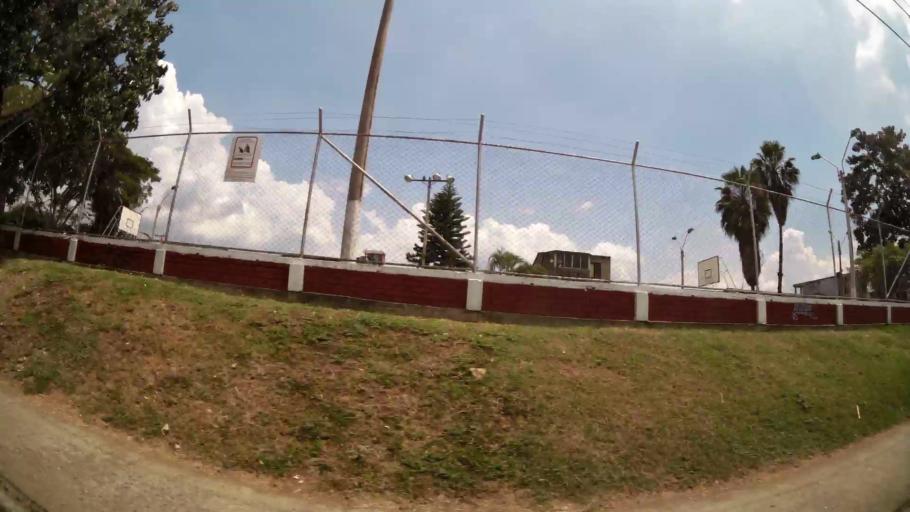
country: CO
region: Valle del Cauca
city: Cali
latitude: 3.4691
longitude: -76.4842
